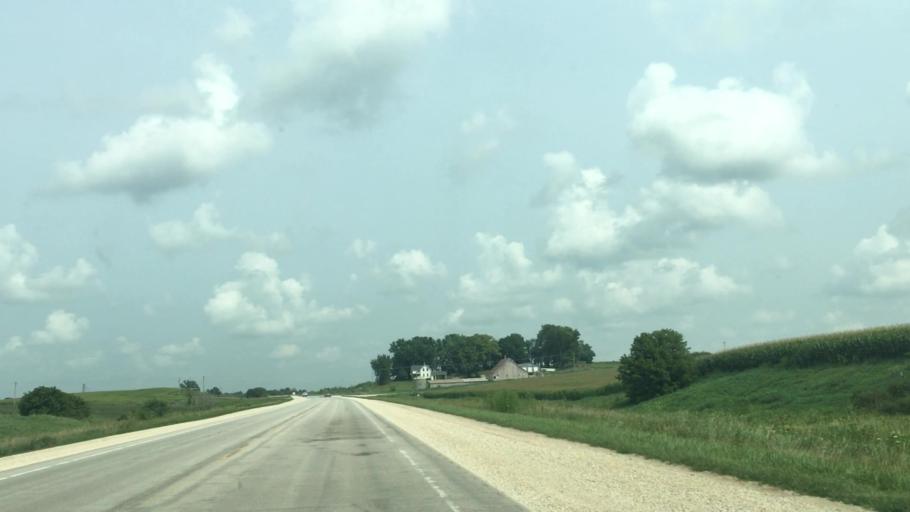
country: US
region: Iowa
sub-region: Winneshiek County
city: Decorah
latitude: 43.3535
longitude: -91.8049
